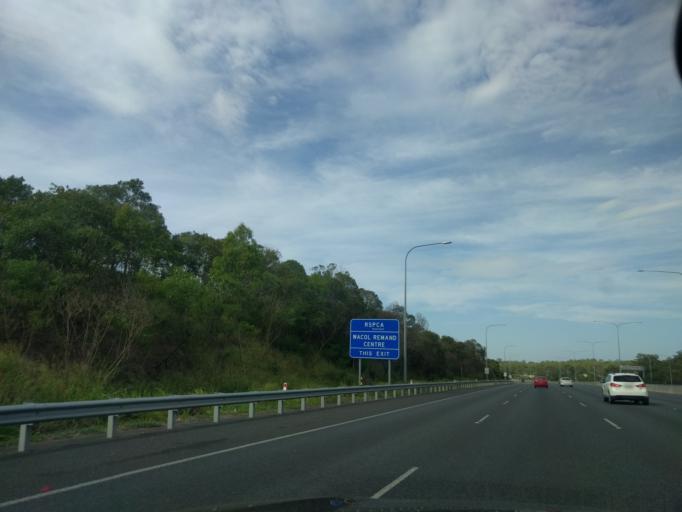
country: AU
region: Queensland
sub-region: Brisbane
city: Wacol
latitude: -27.5827
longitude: 152.9334
